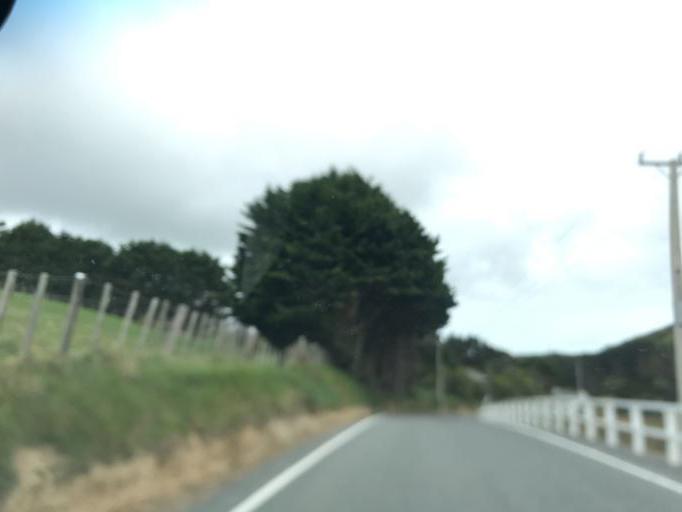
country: NZ
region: Wellington
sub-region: Porirua City
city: Porirua
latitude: -41.1751
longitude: 174.8005
